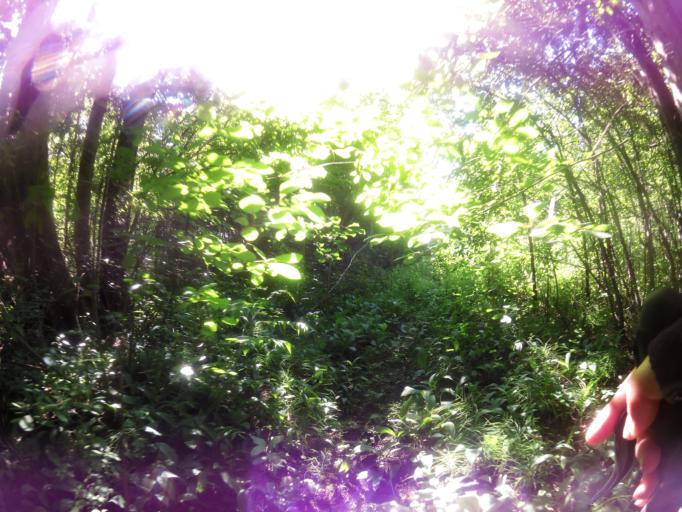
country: CA
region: Ontario
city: Ottawa
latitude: 45.3168
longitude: -75.6974
